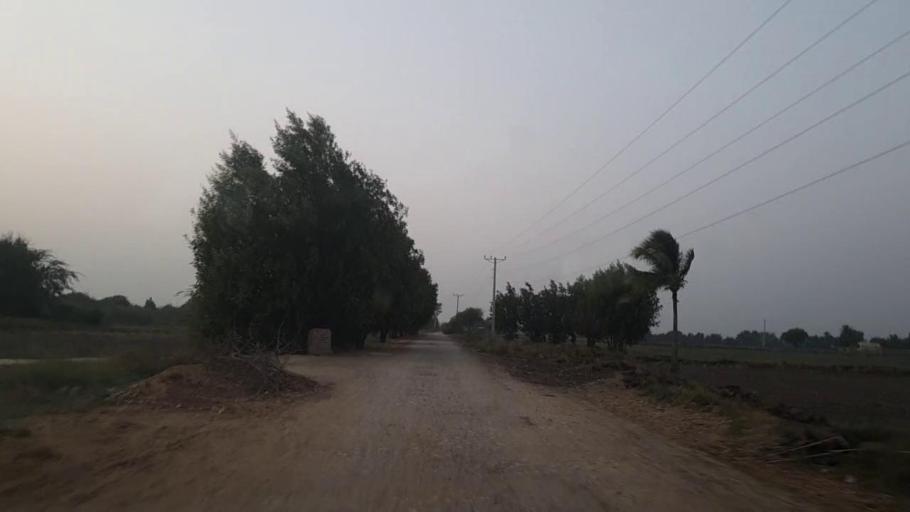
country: PK
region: Sindh
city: Mirpur Sakro
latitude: 24.5918
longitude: 67.7796
